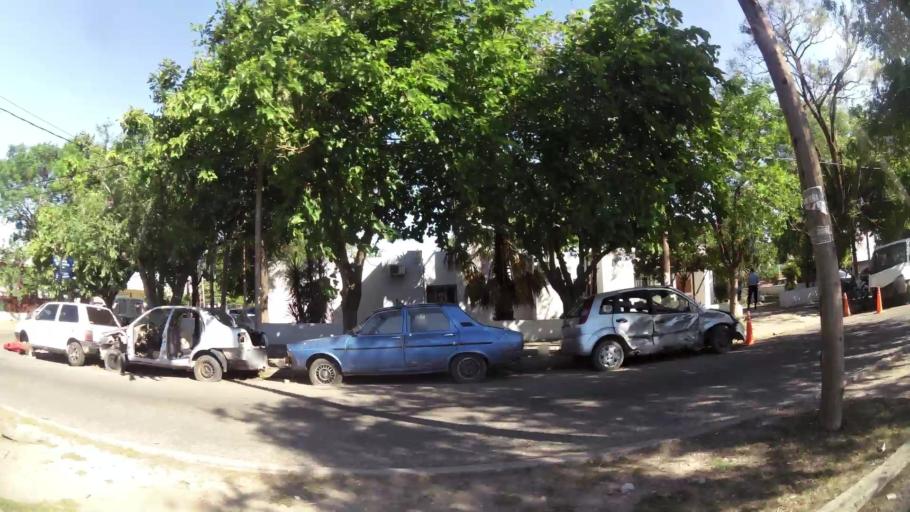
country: AR
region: Cordoba
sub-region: Departamento de Capital
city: Cordoba
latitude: -31.3623
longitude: -64.1957
